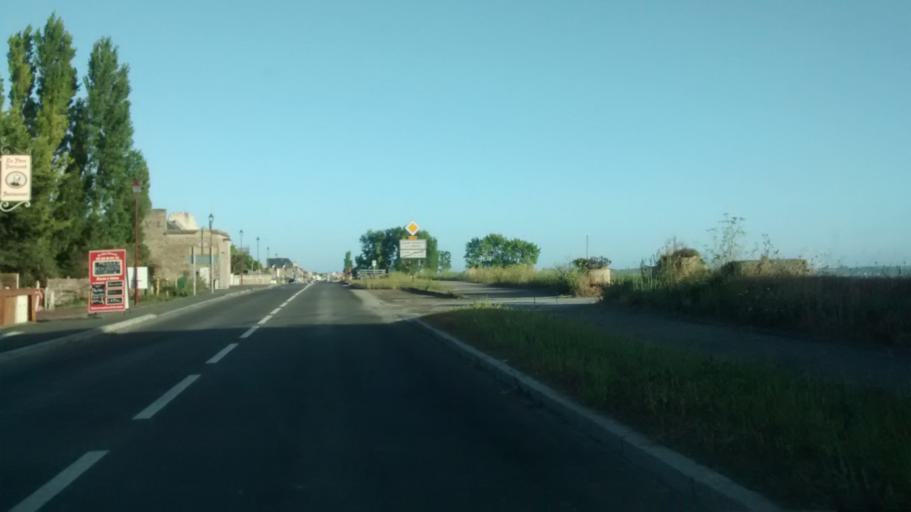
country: FR
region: Brittany
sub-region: Departement d'Ille-et-Vilaine
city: La Fresnais
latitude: 48.6157
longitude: -1.8447
